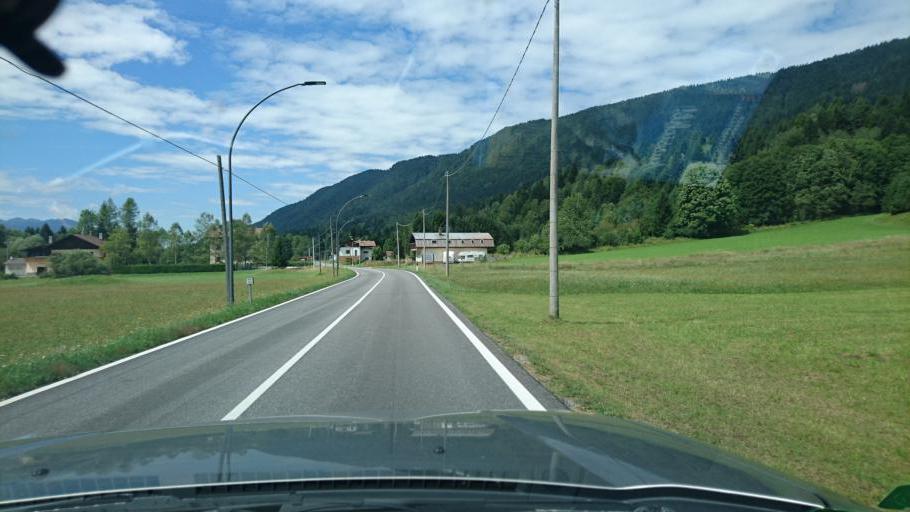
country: AT
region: Carinthia
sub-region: Politischer Bezirk Villach Land
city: Arnoldstein
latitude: 46.4982
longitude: 13.6939
